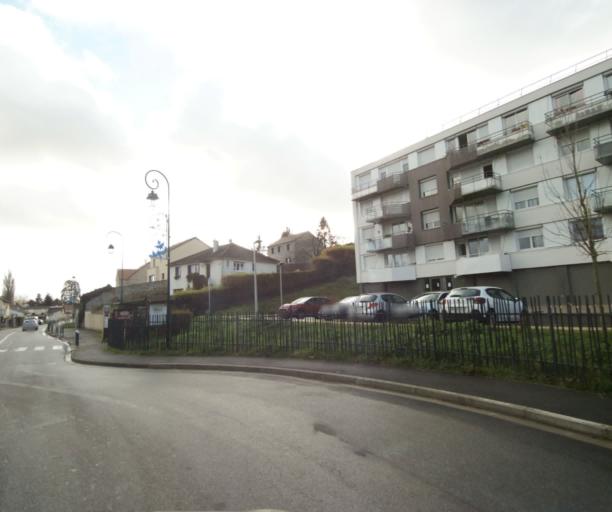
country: FR
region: Ile-de-France
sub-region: Departement des Yvelines
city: Hardricourt
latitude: 49.0144
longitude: 1.8987
